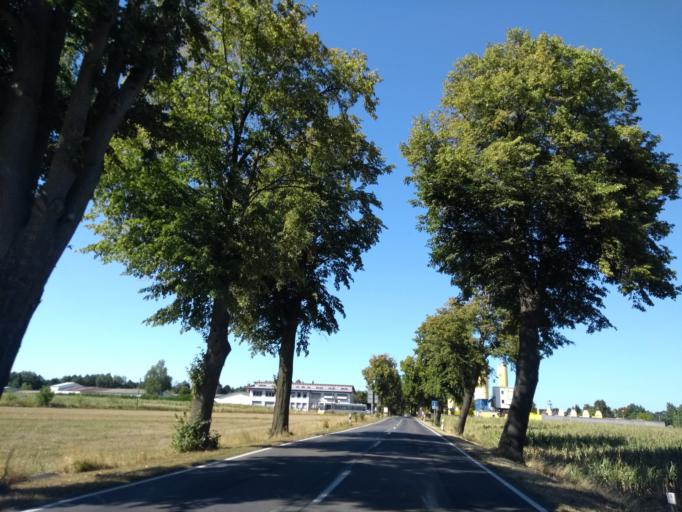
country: DE
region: Brandenburg
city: Lubbenau
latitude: 51.8381
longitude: 13.9757
